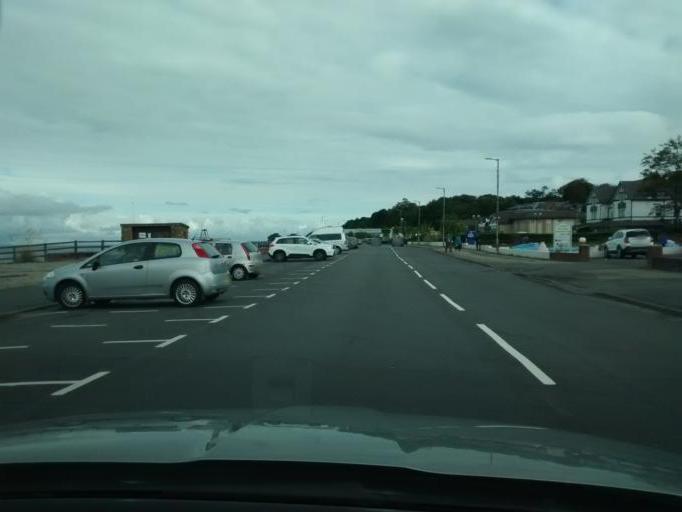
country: GB
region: Scotland
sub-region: North Ayrshire
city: Lamlash
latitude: 55.5770
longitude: -5.1455
